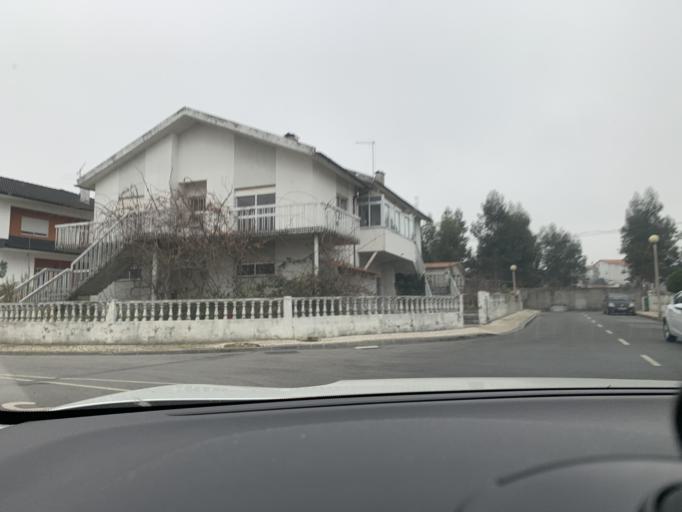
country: PT
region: Viseu
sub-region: Viseu
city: Rio de Loba
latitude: 40.6617
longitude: -7.8890
